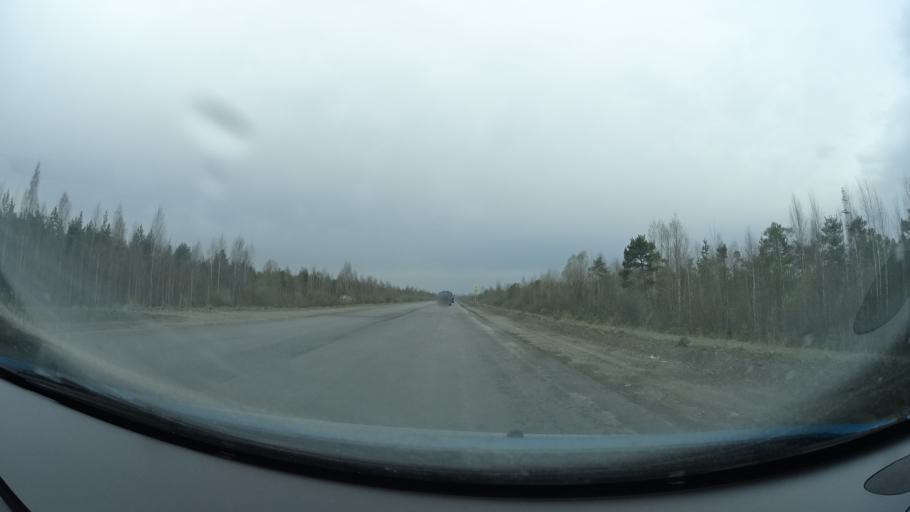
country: RU
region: Perm
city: Krasnokamsk
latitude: 58.0873
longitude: 55.7034
